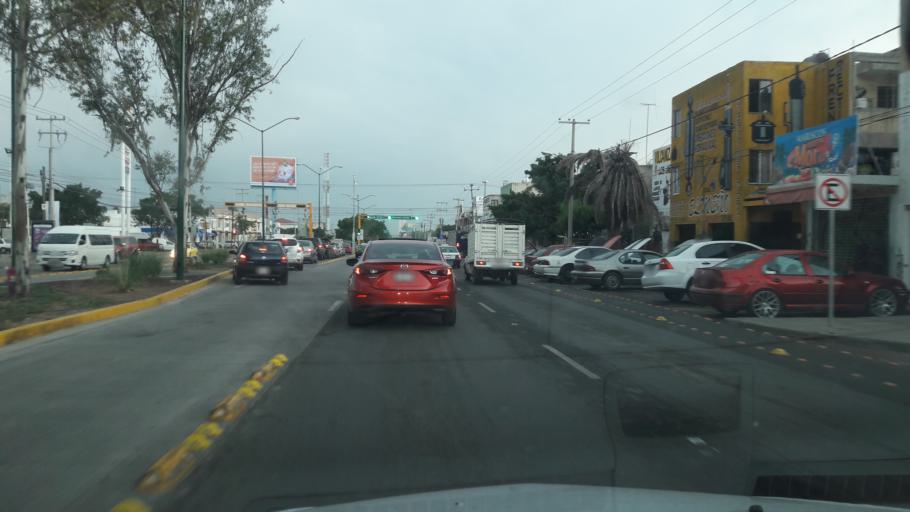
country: MX
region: Guanajuato
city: Leon
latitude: 21.1294
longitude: -101.6462
